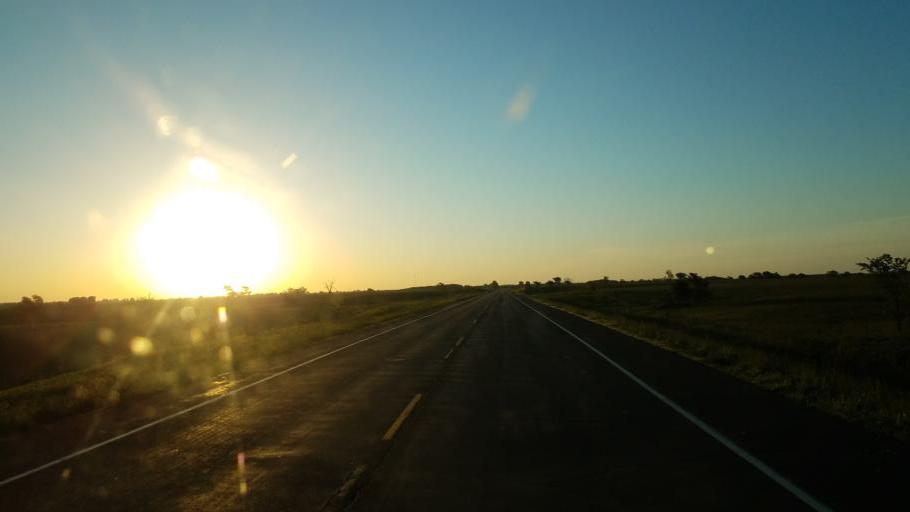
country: US
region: Missouri
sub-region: Schuyler County
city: Lancaster
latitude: 40.4926
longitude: -92.5775
